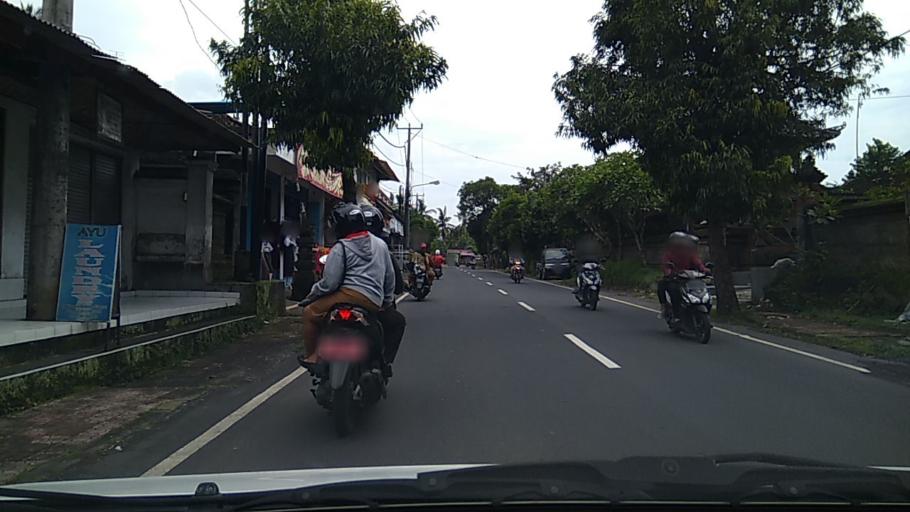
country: ID
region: Bali
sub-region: Kabupaten Gianyar
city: Ubud
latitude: -8.5297
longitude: 115.2986
